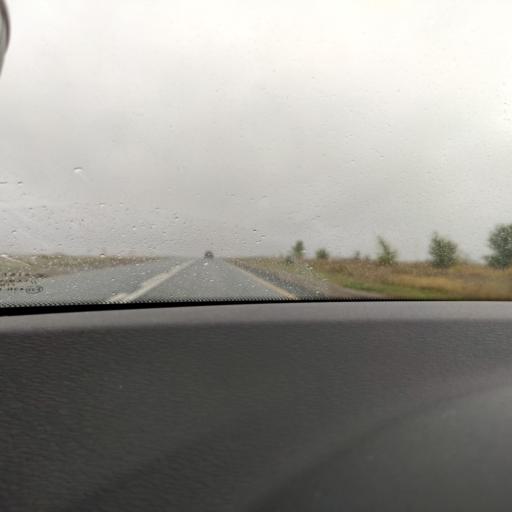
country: RU
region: Samara
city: Novyy Buyan
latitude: 53.6779
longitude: 50.2158
